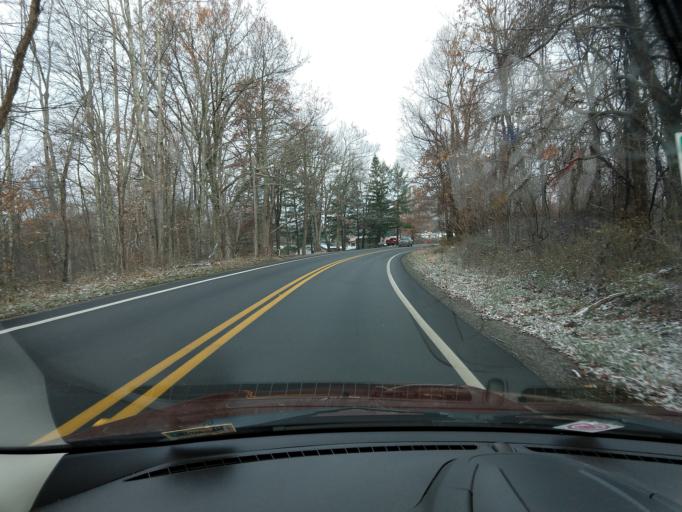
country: US
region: West Virginia
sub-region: Nicholas County
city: Craigsville
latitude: 38.2305
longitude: -80.6968
